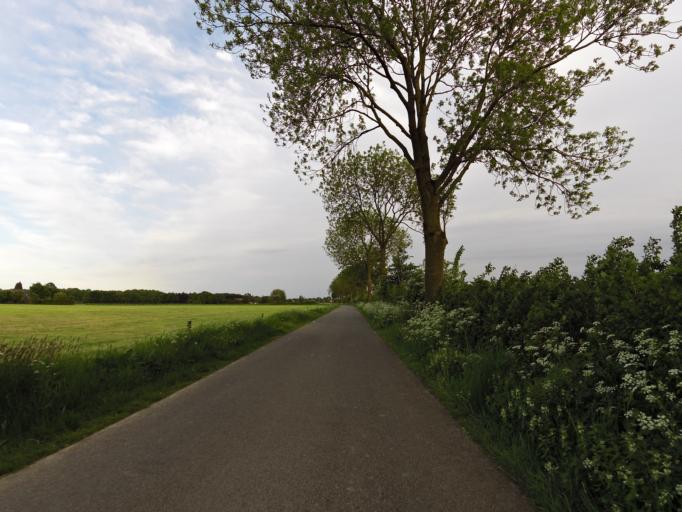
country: NL
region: Gelderland
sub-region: Oude IJsselstreek
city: Gendringen
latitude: 51.8542
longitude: 6.3847
